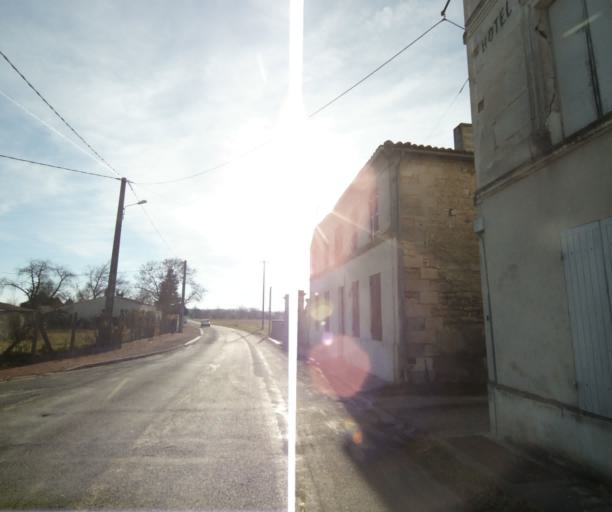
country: FR
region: Poitou-Charentes
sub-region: Departement de la Charente-Maritime
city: Chaniers
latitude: 45.7005
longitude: -0.5281
